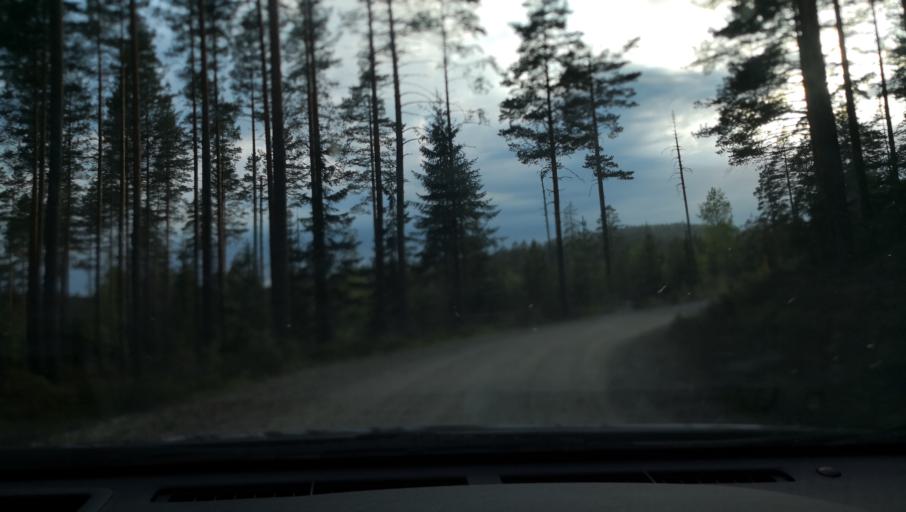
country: SE
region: Vaestmanland
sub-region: Skinnskattebergs Kommun
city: Skinnskatteberg
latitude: 59.7987
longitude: 15.4890
